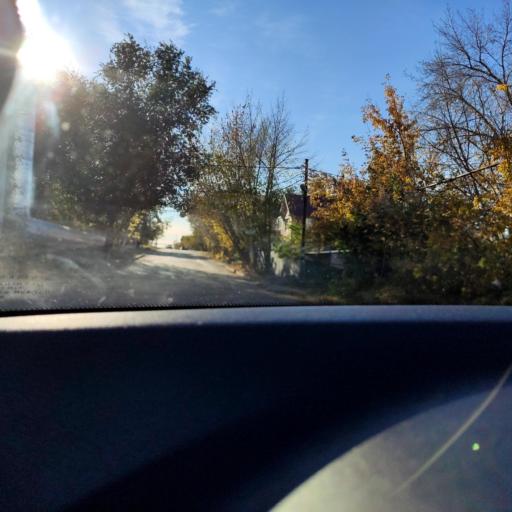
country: RU
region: Samara
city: Samara
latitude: 53.1869
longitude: 50.1563
